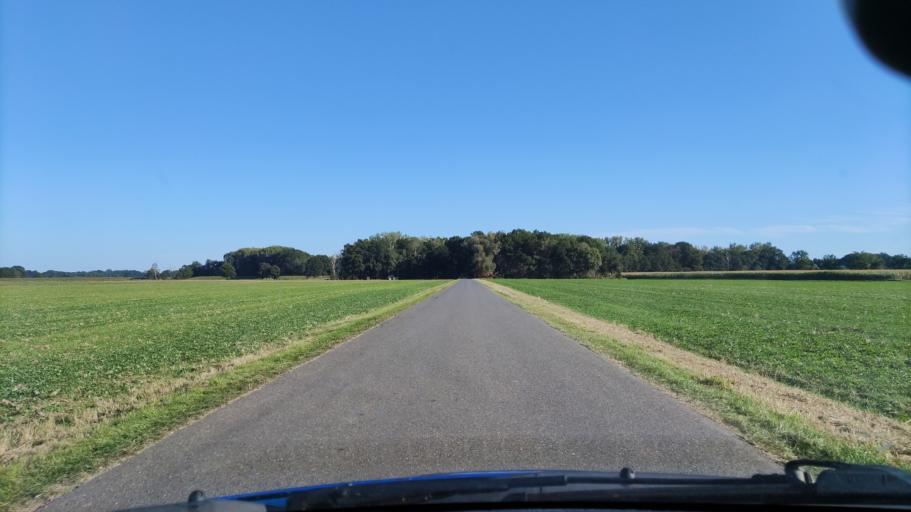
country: DE
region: Lower Saxony
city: Dannenberg
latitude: 53.1273
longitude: 11.0931
